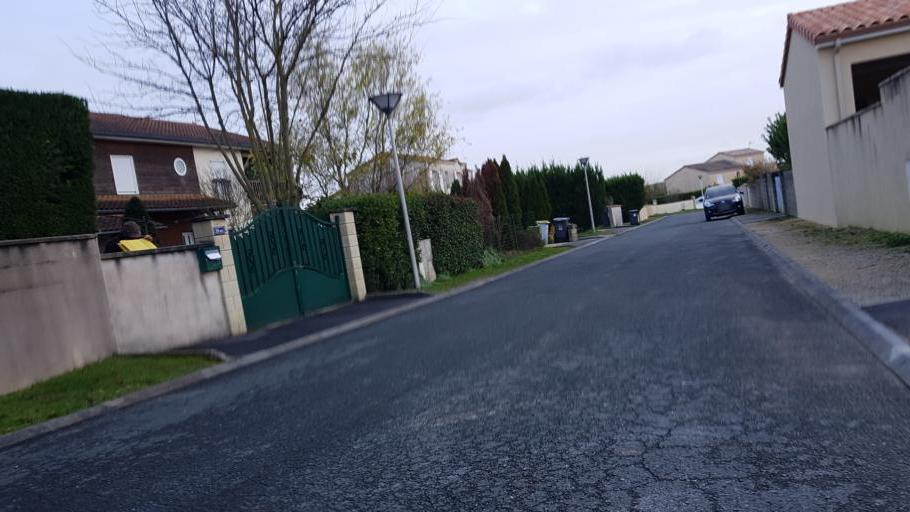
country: FR
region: Poitou-Charentes
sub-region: Departement de la Vienne
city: Avanton
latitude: 46.6614
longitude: 0.3390
